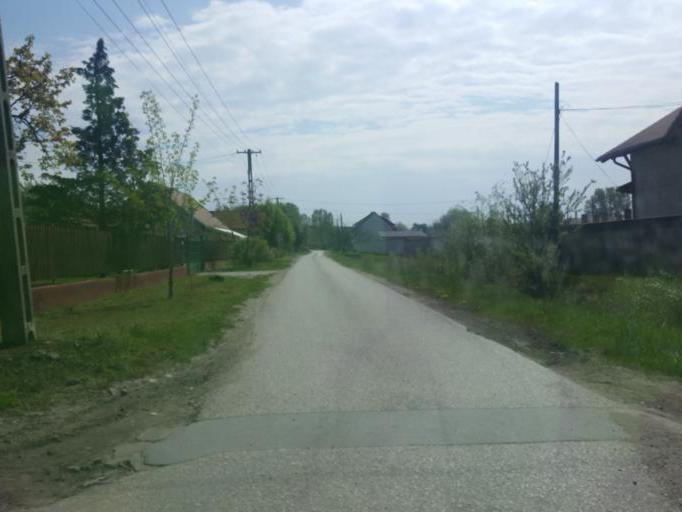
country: HU
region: Pest
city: Monor
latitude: 47.3334
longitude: 19.4467
